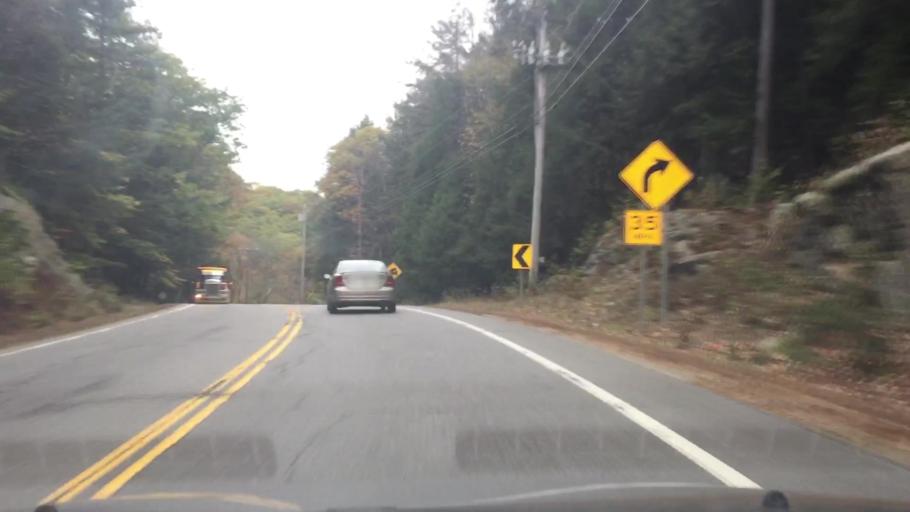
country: US
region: New Hampshire
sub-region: Cheshire County
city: Keene
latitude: 43.0273
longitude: -72.2684
